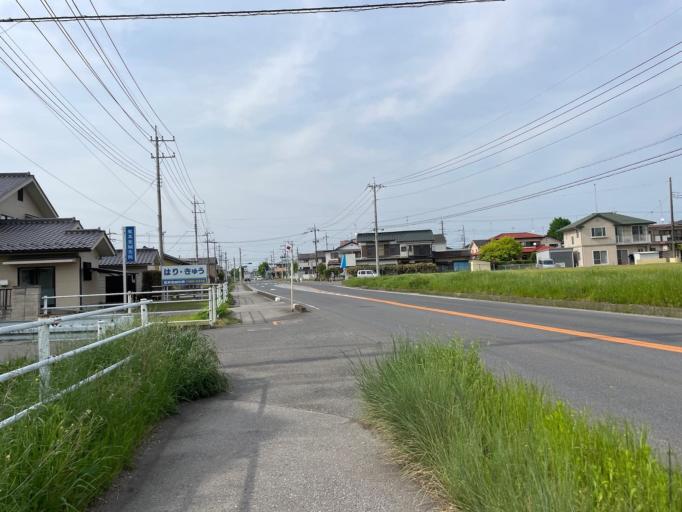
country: JP
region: Tochigi
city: Mibu
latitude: 36.4119
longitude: 139.8044
